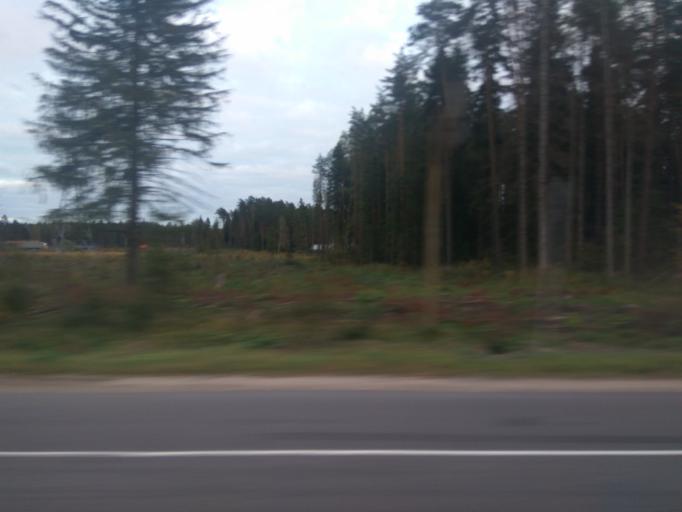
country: RU
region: Moskovskaya
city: Krasnoarmeysk
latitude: 56.0369
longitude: 38.1964
